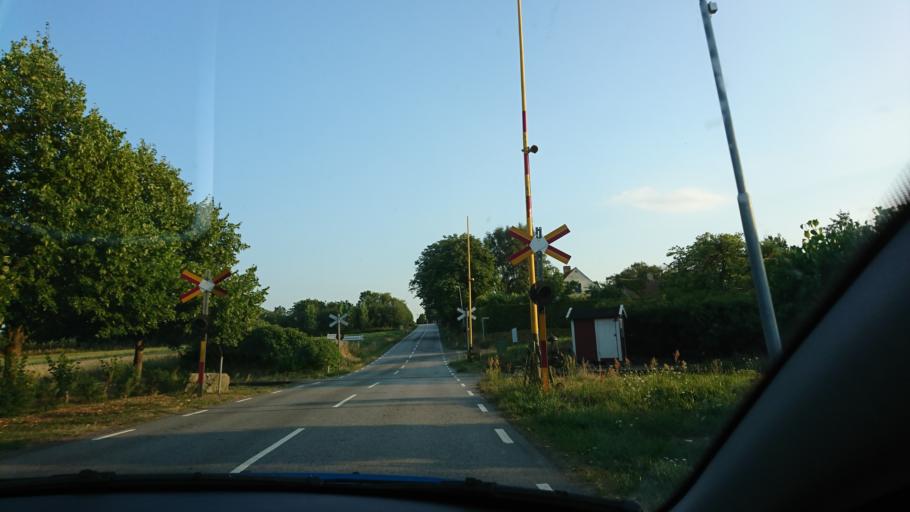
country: SE
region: Skane
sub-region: Simrishamns Kommun
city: Kivik
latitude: 55.7082
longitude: 14.1519
